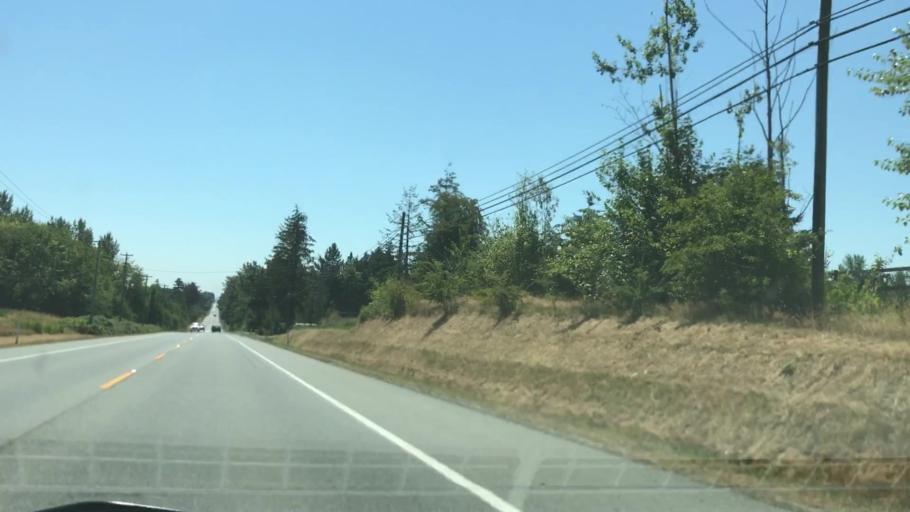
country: CA
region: British Columbia
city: Aldergrove
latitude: 49.0515
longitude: -122.4927
